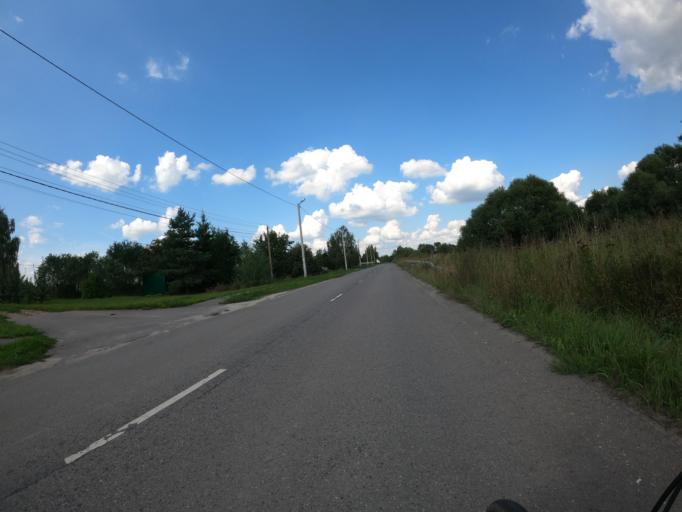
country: RU
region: Moskovskaya
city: Troitskoye
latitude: 55.2520
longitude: 38.5780
